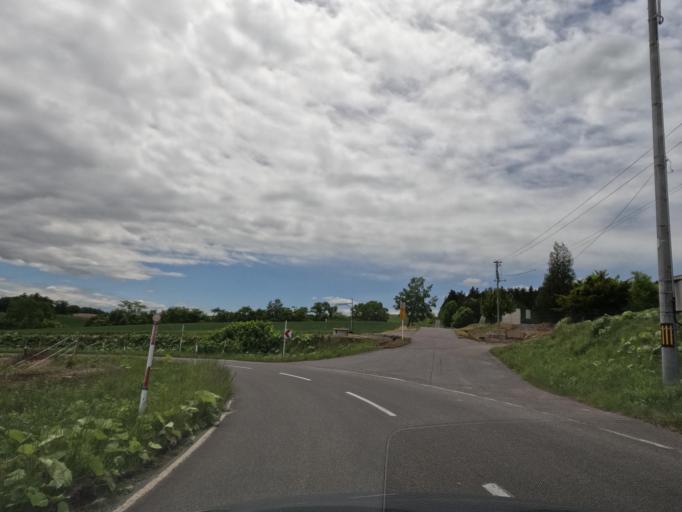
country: JP
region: Hokkaido
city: Shimo-furano
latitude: 43.5003
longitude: 142.4127
